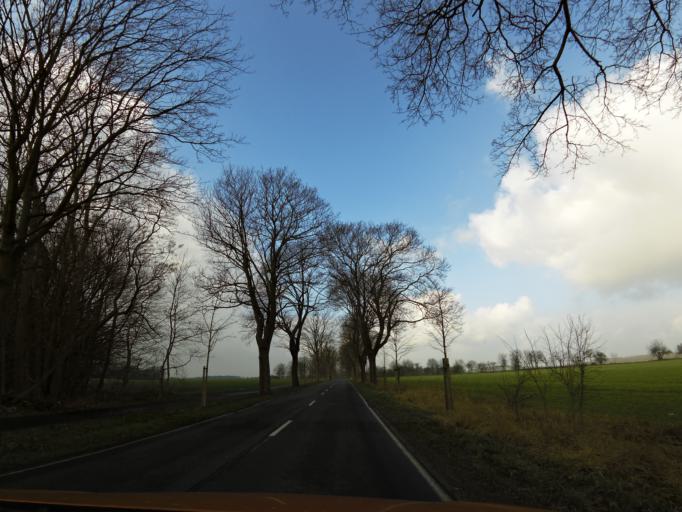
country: DE
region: Berlin
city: Wilhelmstadt
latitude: 52.5059
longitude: 13.1623
